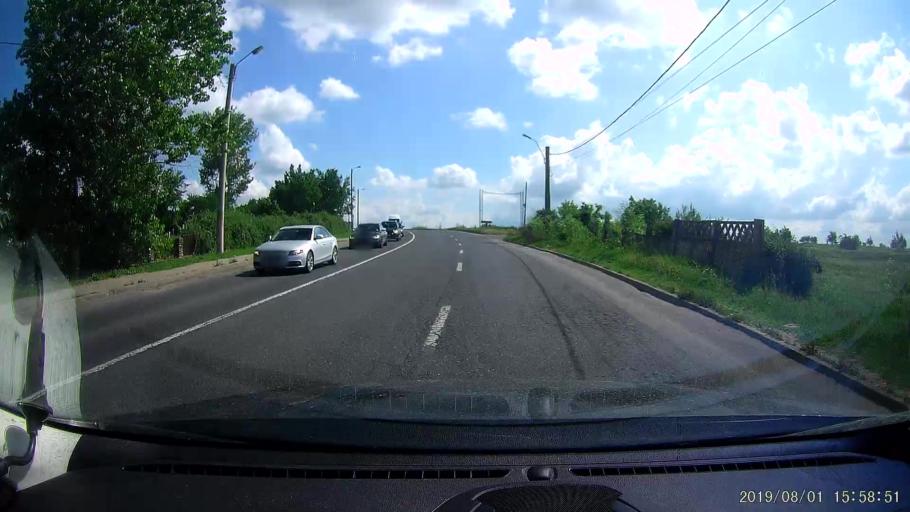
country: RO
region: Ialomita
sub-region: Comuna Slobozia
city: Slobozia
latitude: 44.5593
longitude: 27.3811
